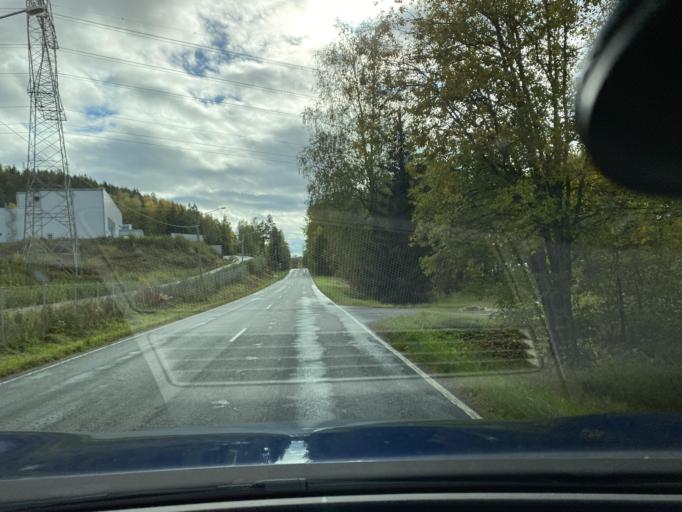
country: FI
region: Pirkanmaa
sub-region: Tampere
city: Nokia
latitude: 61.4899
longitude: 23.3437
